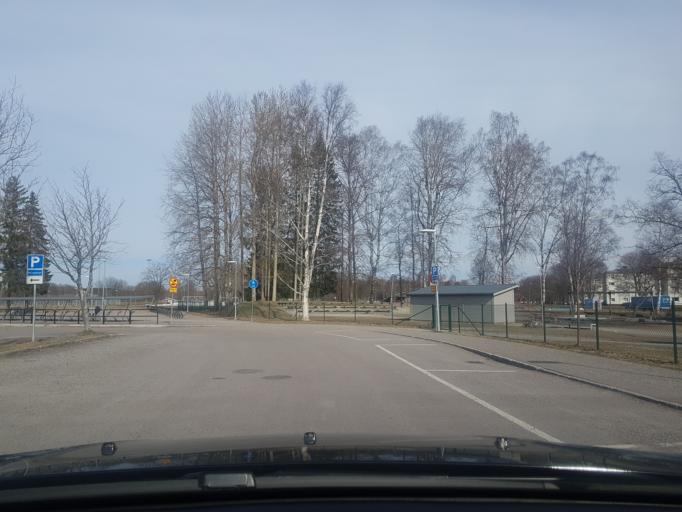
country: SE
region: Dalarna
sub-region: Borlange Kommun
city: Borlaenge
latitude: 60.4926
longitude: 15.4143
